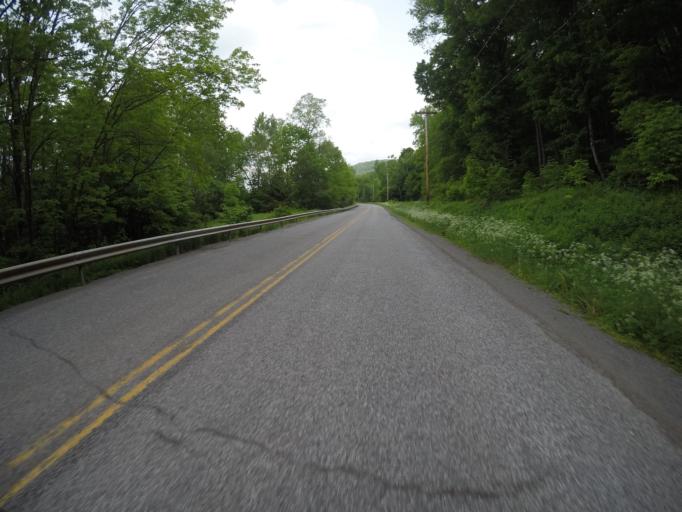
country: US
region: New York
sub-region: Delaware County
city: Delhi
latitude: 42.1541
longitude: -74.6867
